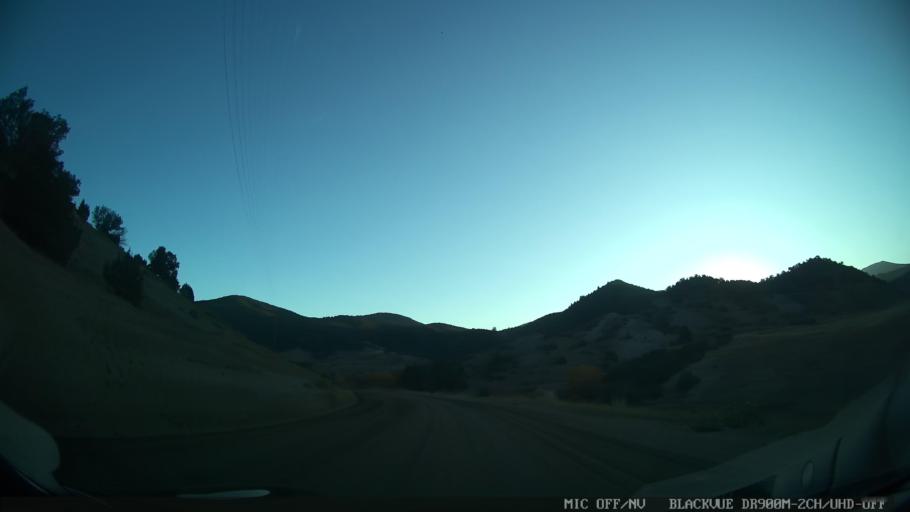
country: US
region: Colorado
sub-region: Grand County
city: Kremmling
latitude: 39.9265
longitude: -106.5314
